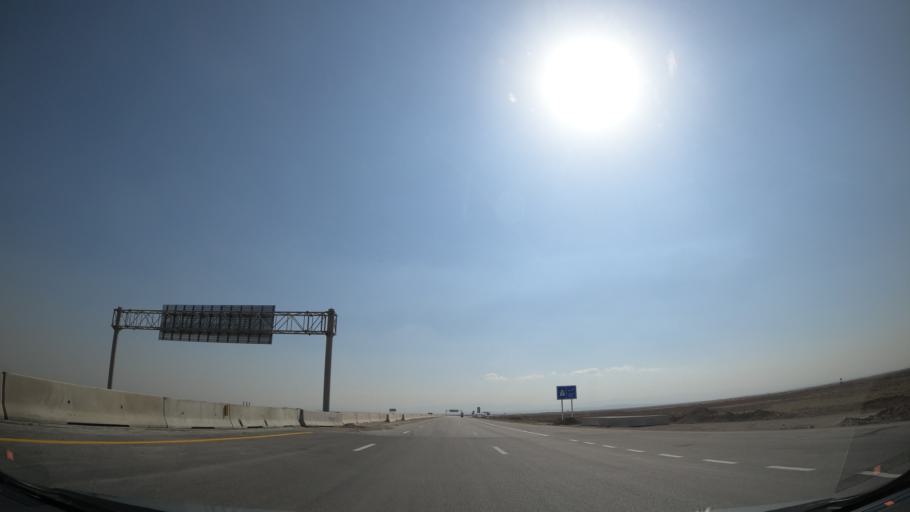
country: IR
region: Qazvin
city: Abyek
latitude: 35.9563
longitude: 50.4653
